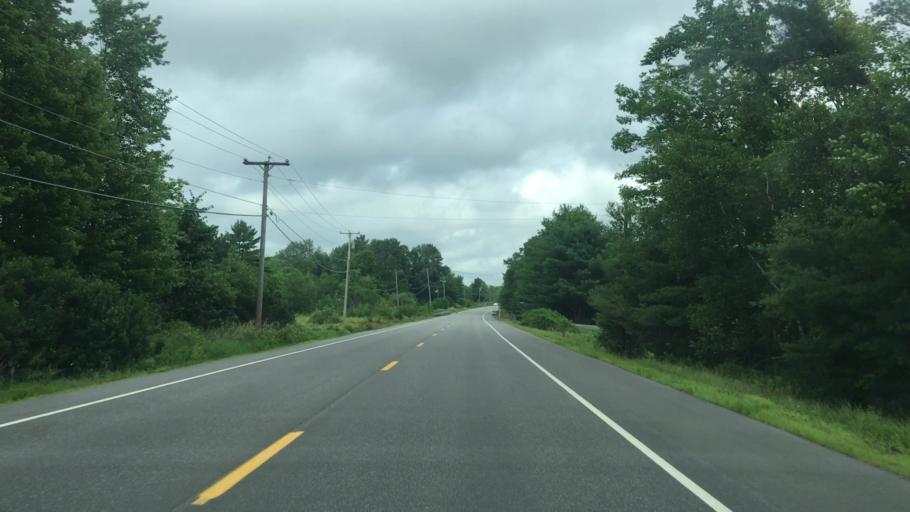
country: US
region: Maine
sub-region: Kennebec County
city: Pittston
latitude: 44.2081
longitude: -69.7546
